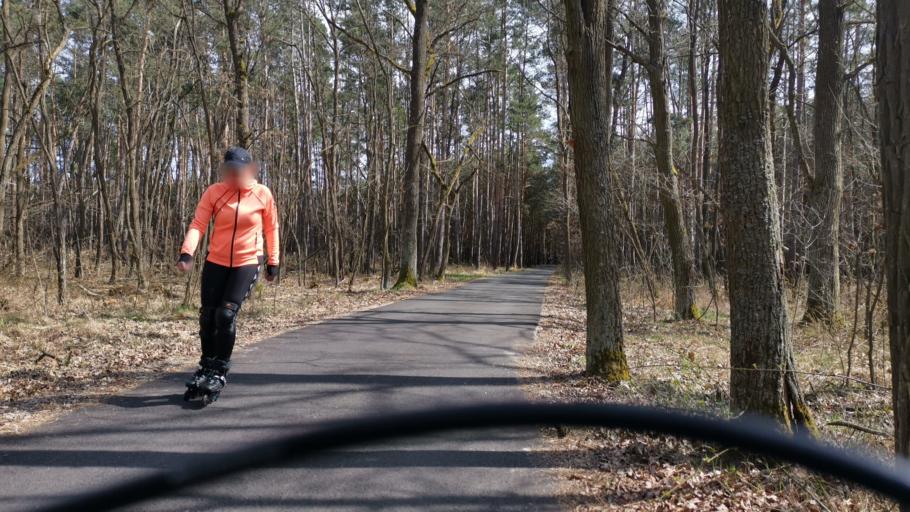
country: CZ
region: South Moravian
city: Tvrdonice
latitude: 48.7217
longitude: 17.0474
